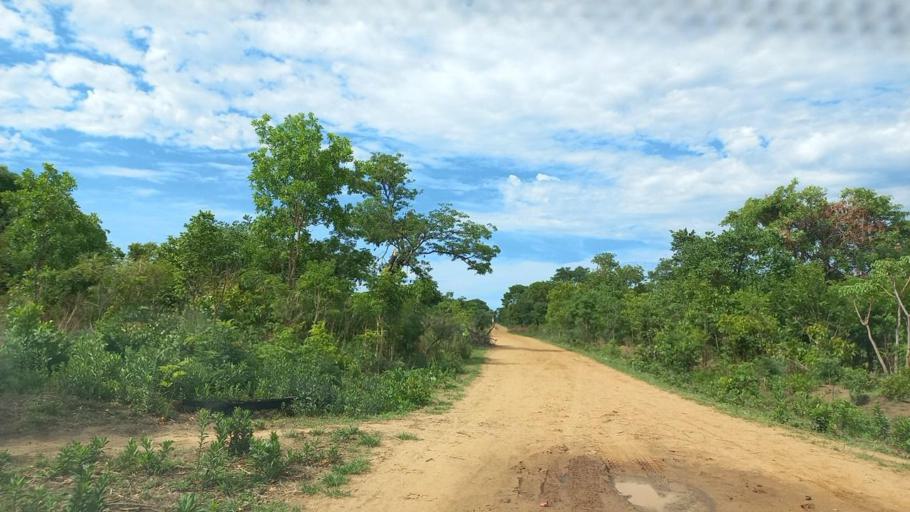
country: ZM
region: North-Western
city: Kabompo
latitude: -13.5246
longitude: 24.3814
